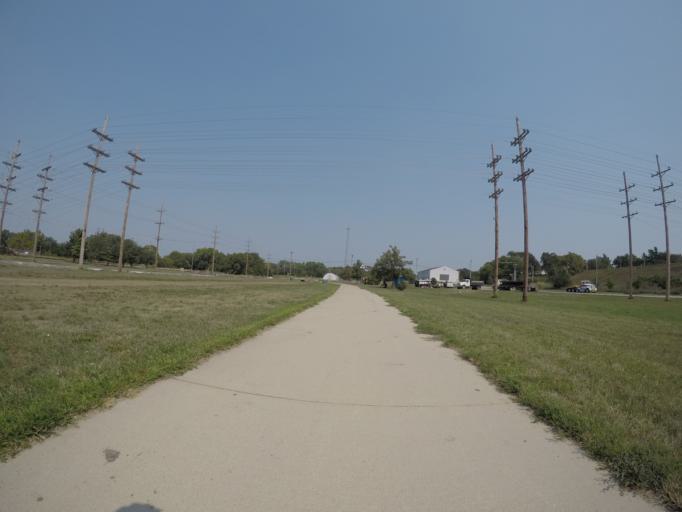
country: US
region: Nebraska
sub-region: Gage County
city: Beatrice
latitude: 40.2696
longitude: -96.7518
